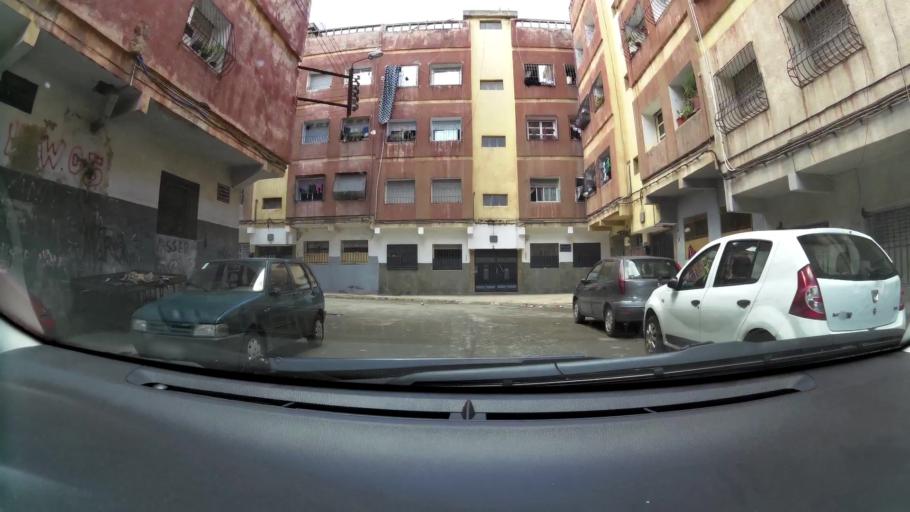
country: MA
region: Grand Casablanca
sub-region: Mediouna
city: Tit Mellil
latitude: 33.5370
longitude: -7.5527
